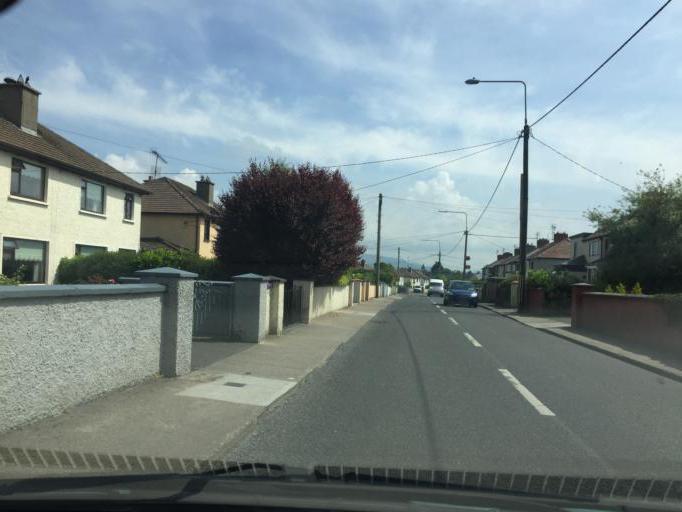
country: IE
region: Connaught
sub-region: Sligo
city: Sligo
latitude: 54.2665
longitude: -8.4998
